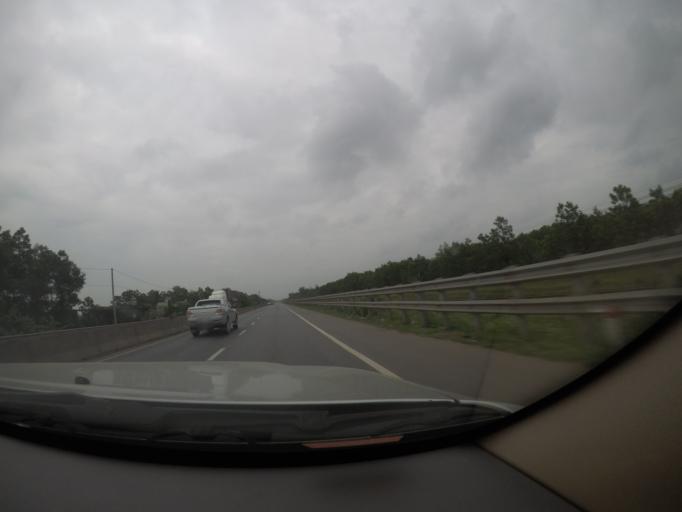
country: VN
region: Quang Tri
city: Hai Lang
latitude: 16.6463
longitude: 107.2897
